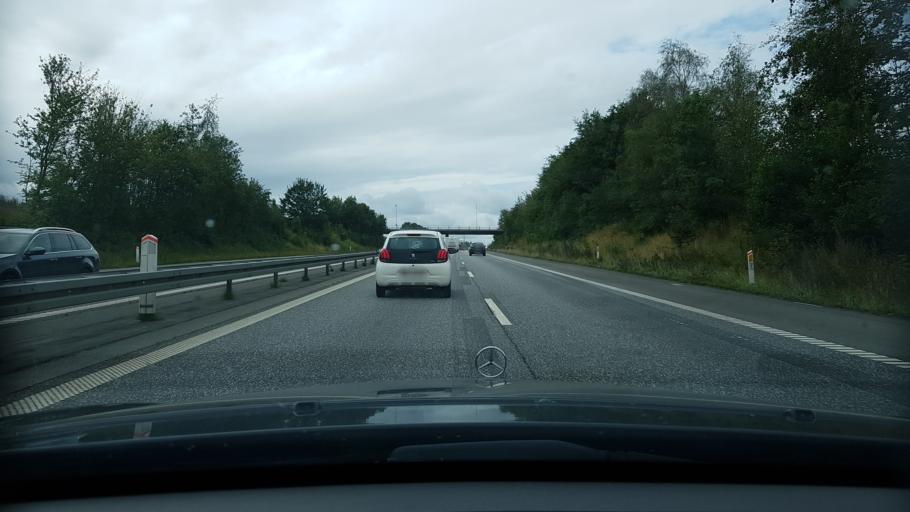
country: DK
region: Central Jutland
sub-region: Horsens Kommune
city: Horsens
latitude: 55.8685
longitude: 9.7685
